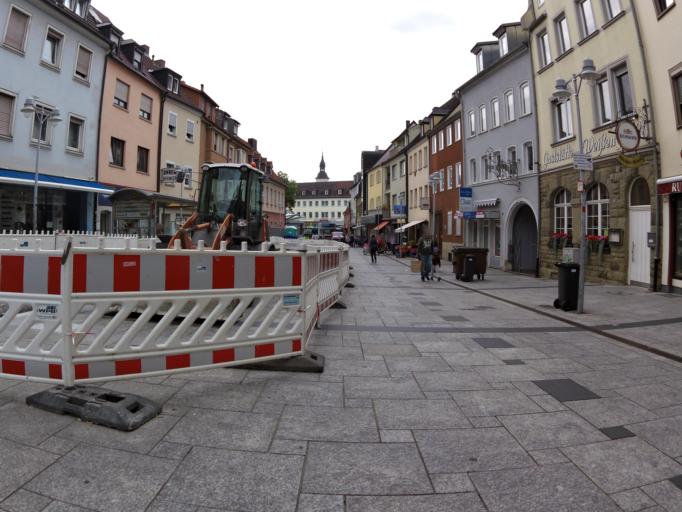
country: DE
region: Bavaria
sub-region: Regierungsbezirk Unterfranken
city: Schweinfurt
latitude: 50.0447
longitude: 10.2293
